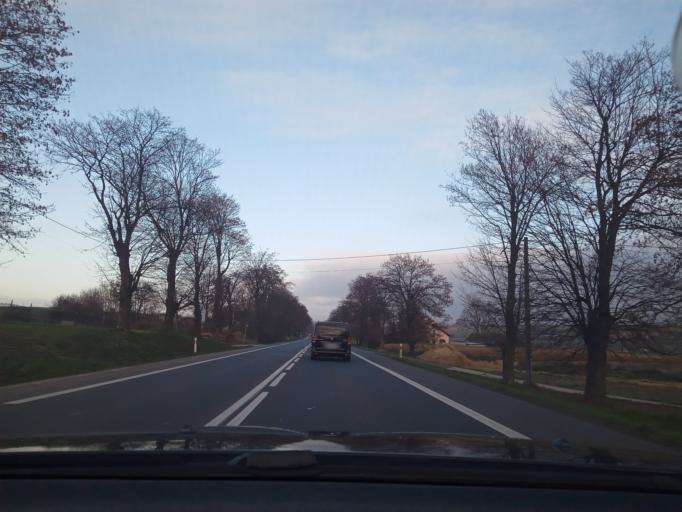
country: PL
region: Lesser Poland Voivodeship
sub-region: Powiat krakowski
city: Slomniki
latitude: 50.2746
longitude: 20.0664
